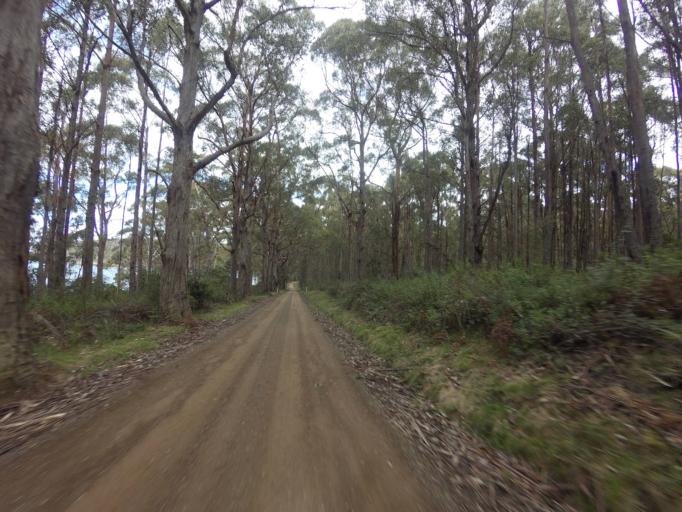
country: AU
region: Tasmania
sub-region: Huon Valley
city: Geeveston
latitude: -43.4173
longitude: 147.0147
